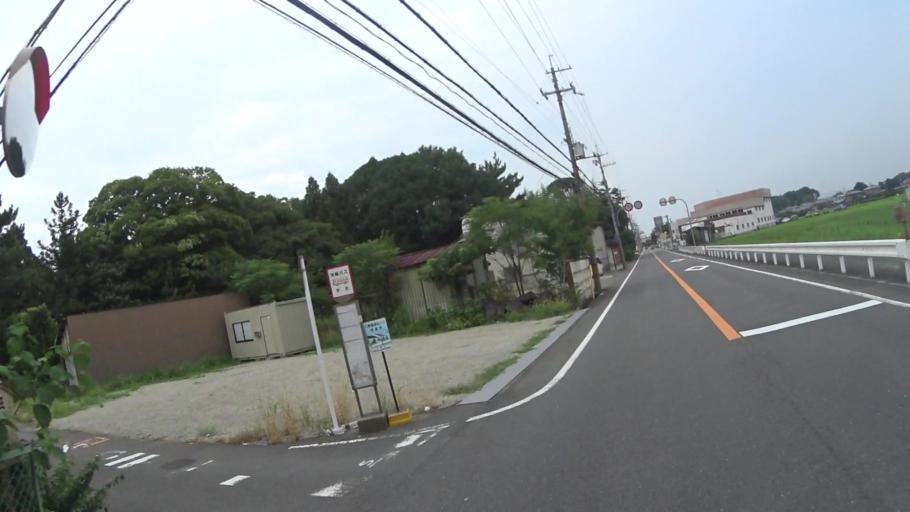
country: JP
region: Kyoto
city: Tanabe
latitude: 34.8603
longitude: 135.7453
